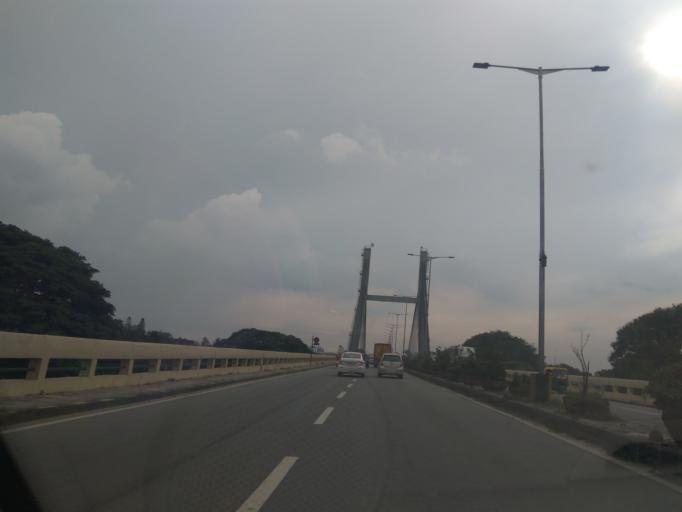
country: IN
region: Karnataka
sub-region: Bangalore Urban
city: Bangalore
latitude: 13.0019
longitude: 77.6796
